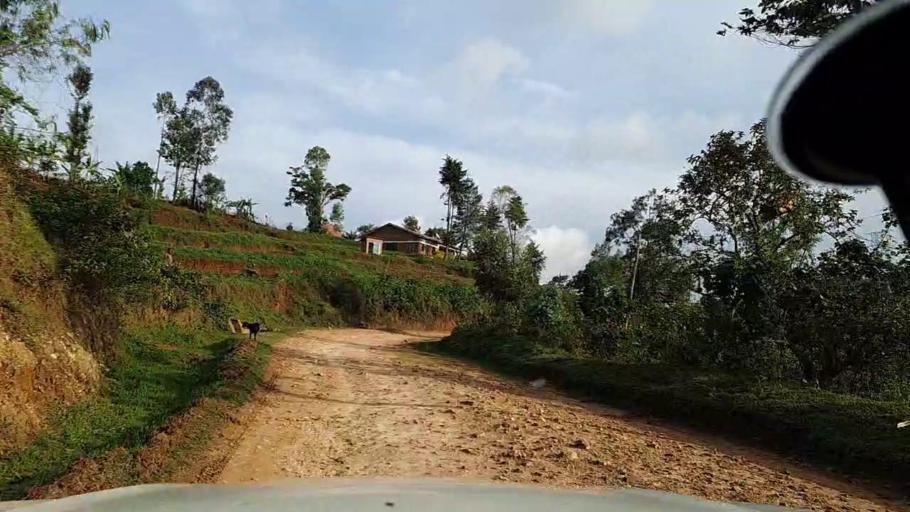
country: RW
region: Southern Province
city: Gitarama
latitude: -2.1844
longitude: 29.5643
